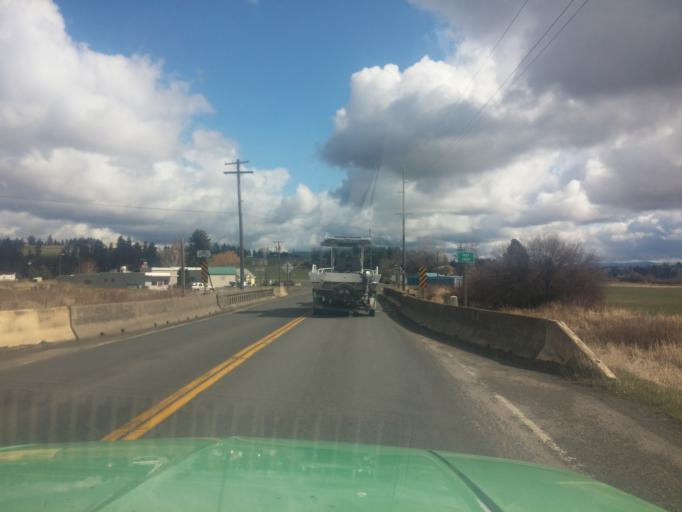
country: US
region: Idaho
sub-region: Latah County
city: Moscow
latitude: 46.9278
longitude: -116.9358
